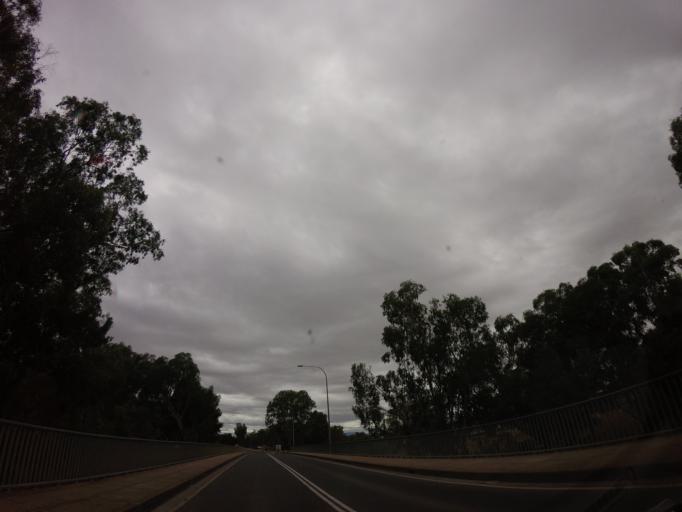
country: AU
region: New South Wales
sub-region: Narrabri
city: Narrabri
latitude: -30.3334
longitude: 149.7724
